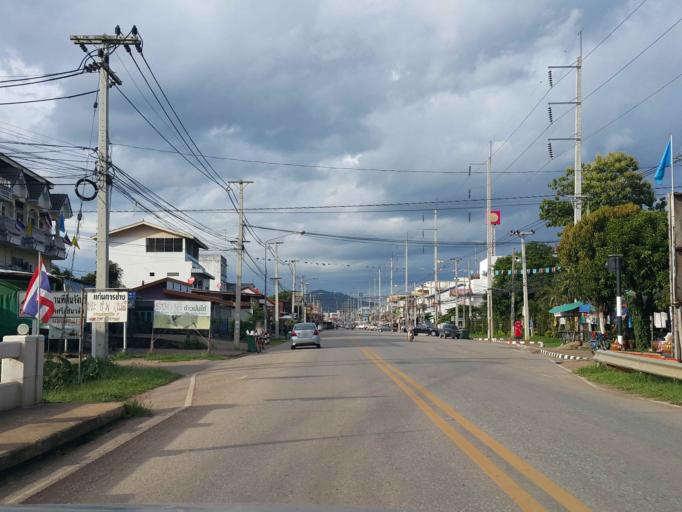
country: TH
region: Sukhothai
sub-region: Amphoe Si Satchanalai
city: Si Satchanalai
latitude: 17.5146
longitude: 99.7612
